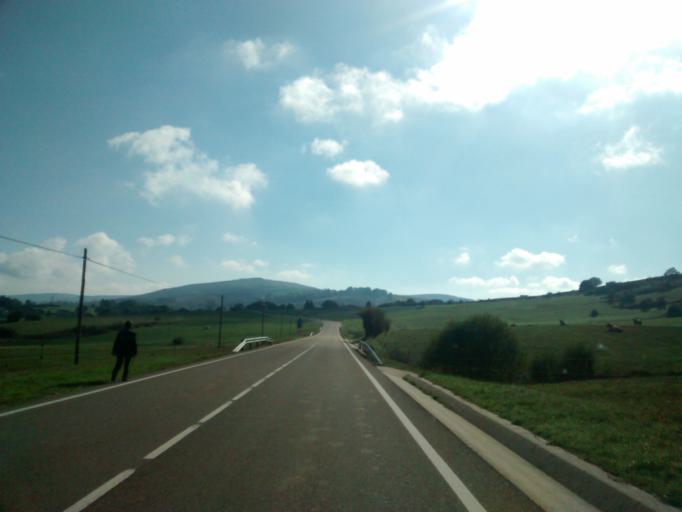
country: ES
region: Cantabria
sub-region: Provincia de Cantabria
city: Reinosa
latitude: 42.9694
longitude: -4.0699
